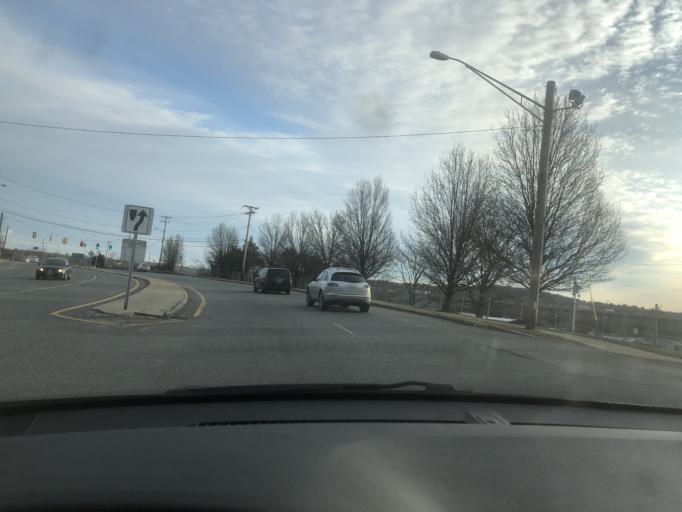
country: US
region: Massachusetts
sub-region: Essex County
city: North Andover
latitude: 42.7073
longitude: -71.1439
